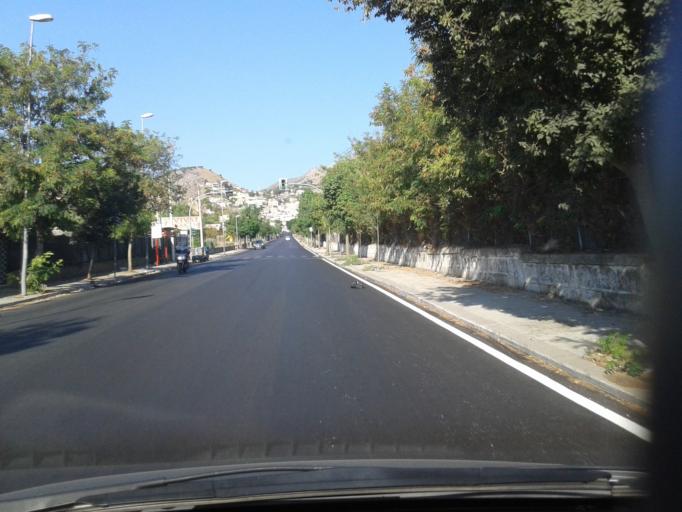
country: IT
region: Sicily
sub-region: Palermo
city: Palermo
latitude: 38.1099
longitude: 13.3164
